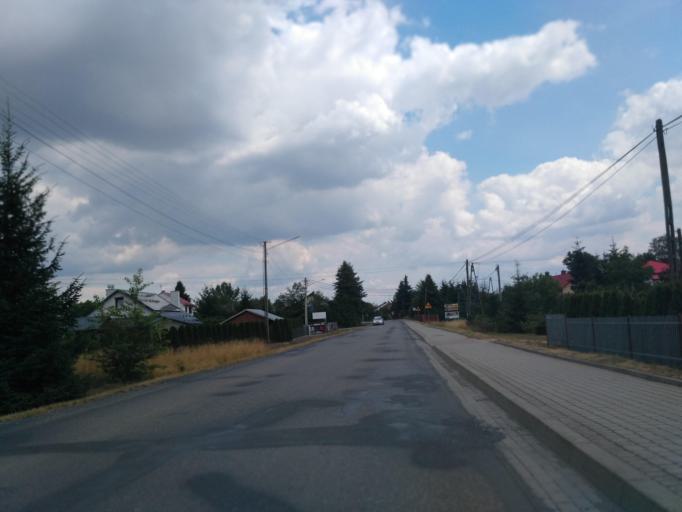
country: PL
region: Subcarpathian Voivodeship
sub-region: Powiat debicki
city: Pilzno
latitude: 50.0421
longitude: 21.3311
